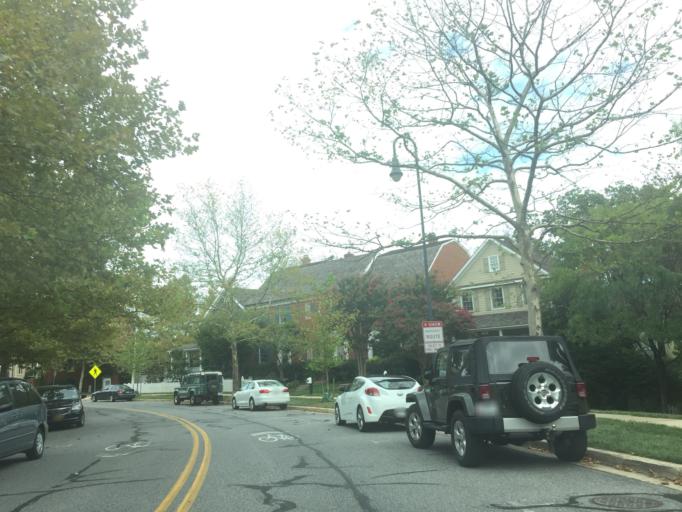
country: US
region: Maryland
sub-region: Montgomery County
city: North Potomac
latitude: 39.1225
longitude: -77.2435
